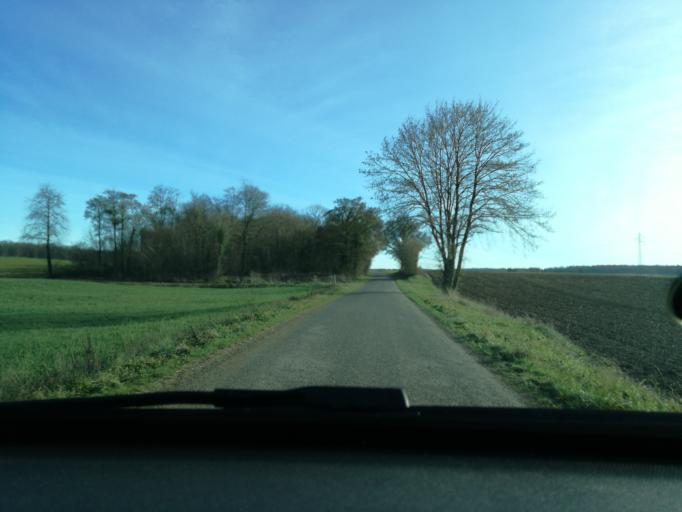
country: FR
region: Lorraine
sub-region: Departement de la Meuse
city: Fains-Veel
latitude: 48.8175
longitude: 5.0653
